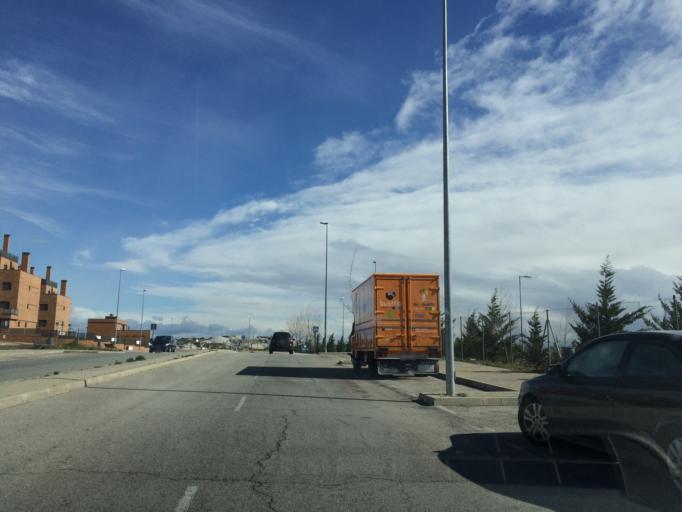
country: ES
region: Madrid
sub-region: Provincia de Madrid
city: Colmenar Viejo
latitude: 40.6601
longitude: -3.7571
